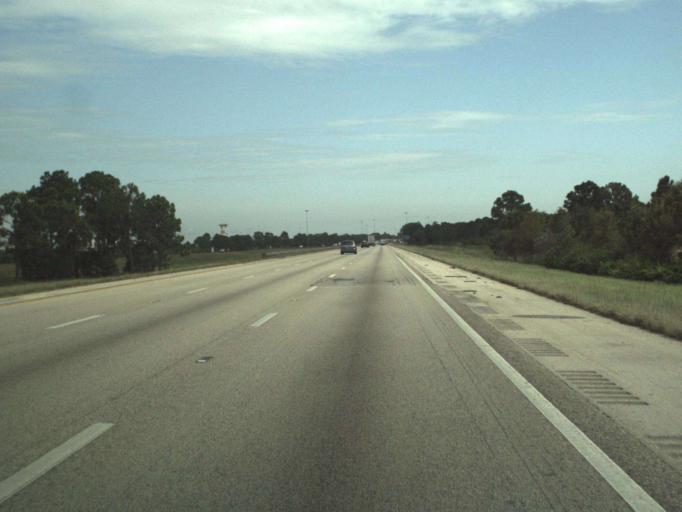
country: US
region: Florida
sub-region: Saint Lucie County
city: Port Saint Lucie
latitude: 27.2499
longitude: -80.4159
